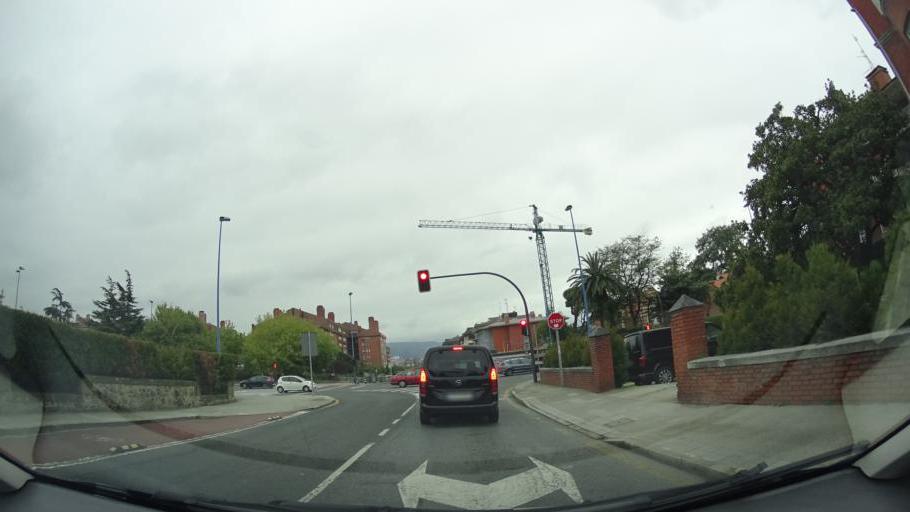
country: ES
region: Basque Country
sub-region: Bizkaia
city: Algorta
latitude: 43.3350
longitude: -3.0050
